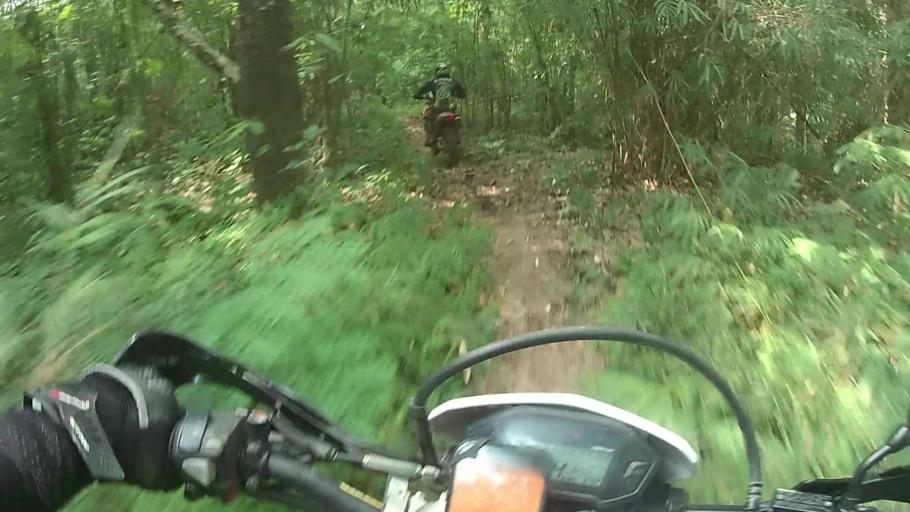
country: TH
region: Chiang Mai
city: Mae Taeng
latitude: 19.0700
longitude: 98.8105
